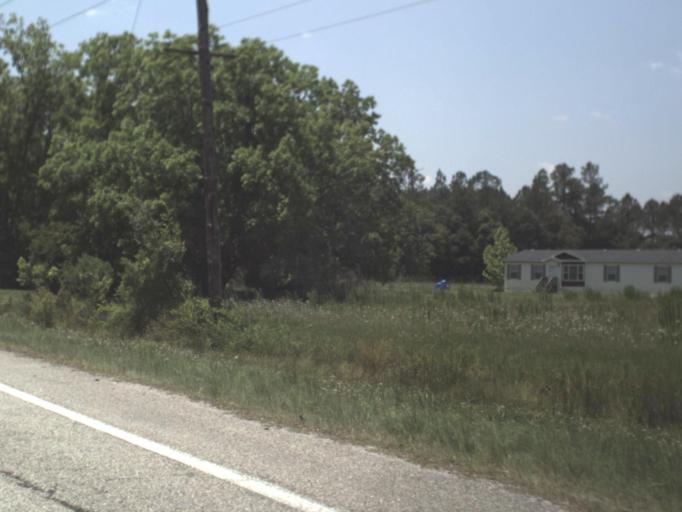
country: US
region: Florida
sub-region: Bradford County
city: Starke
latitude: 30.0751
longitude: -82.0658
